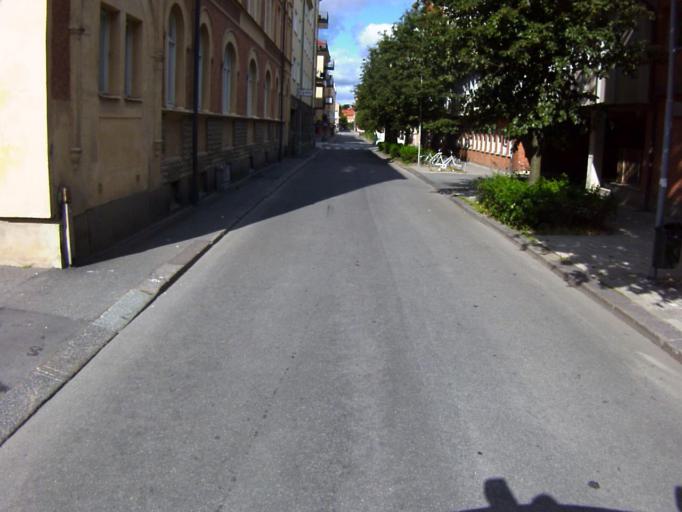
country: SE
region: Soedermanland
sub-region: Eskilstuna Kommun
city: Eskilstuna
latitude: 59.3694
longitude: 16.5096
